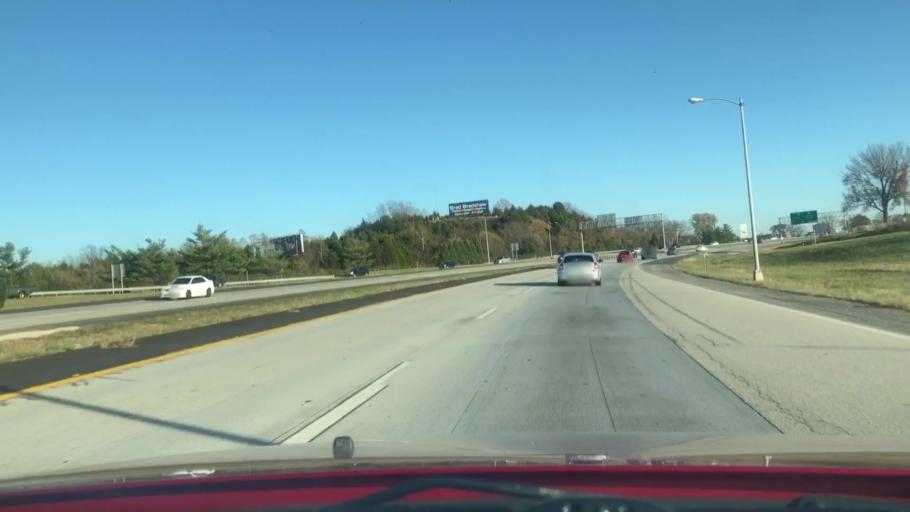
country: US
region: Missouri
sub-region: Greene County
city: Springfield
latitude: 37.1387
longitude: -93.2517
